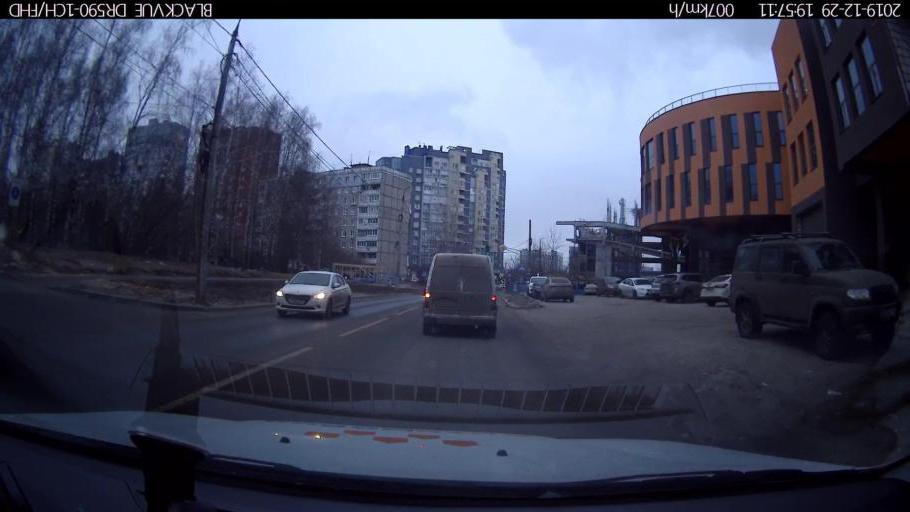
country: RU
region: Nizjnij Novgorod
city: Nizhniy Novgorod
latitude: 56.3076
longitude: 43.9999
